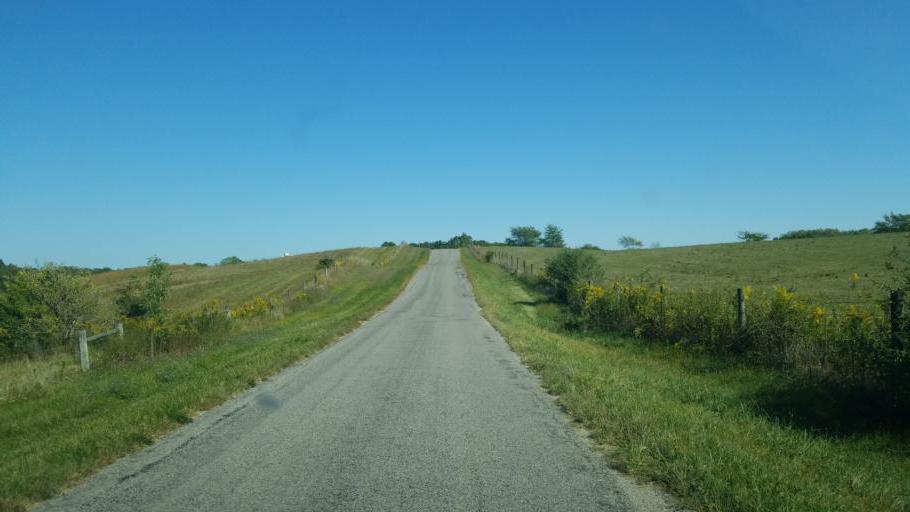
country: US
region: Ohio
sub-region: Champaign County
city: Mechanicsburg
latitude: 40.1146
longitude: -83.5961
